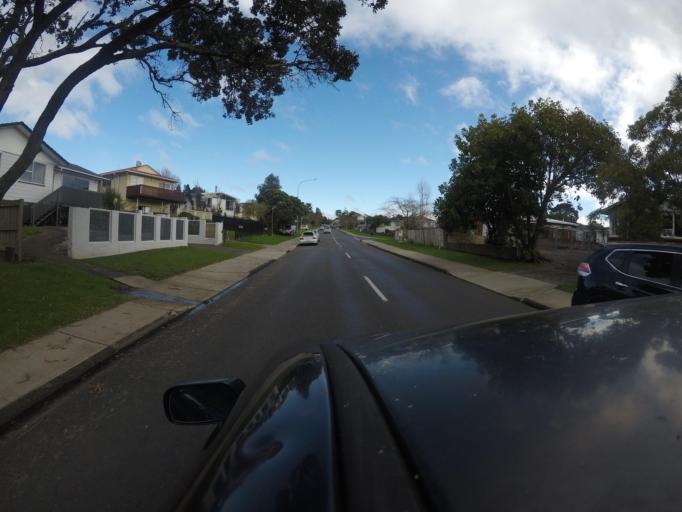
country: NZ
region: Auckland
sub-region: Auckland
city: Waitakere
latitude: -36.8936
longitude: 174.6514
